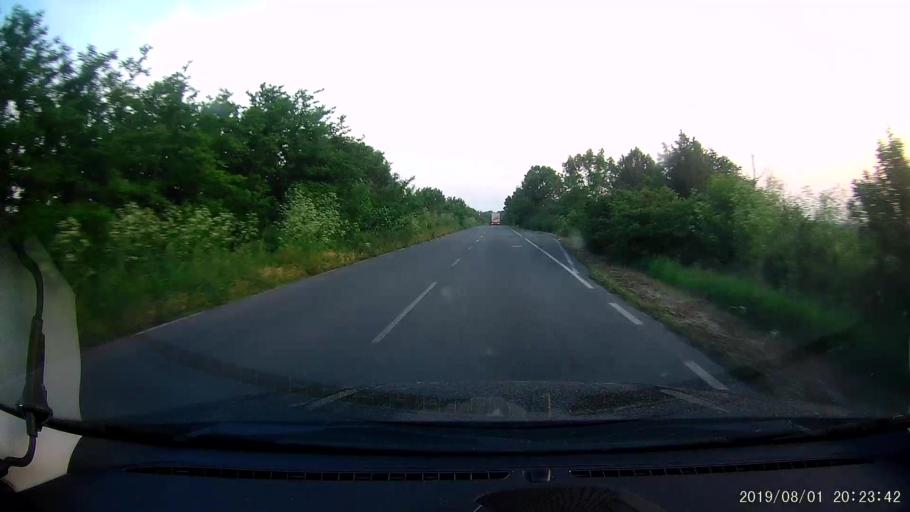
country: BG
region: Yambol
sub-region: Obshtina Elkhovo
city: Elkhovo
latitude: 42.2437
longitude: 26.5984
